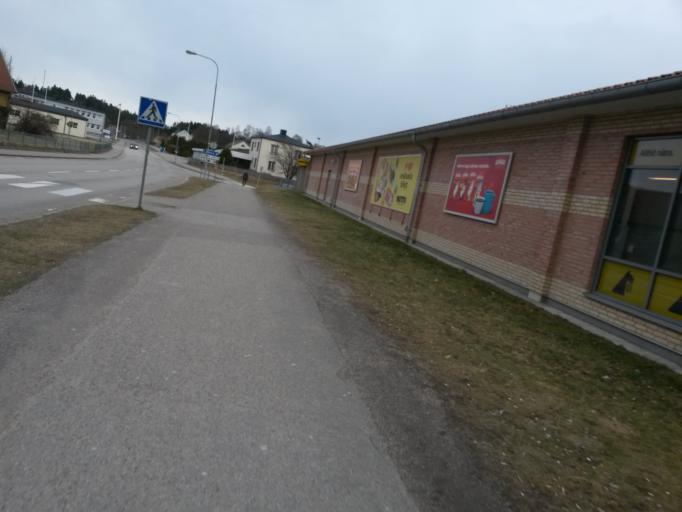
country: SE
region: Vaestra Goetaland
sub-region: Vargarda Kommun
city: Vargarda
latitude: 58.0318
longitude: 12.8124
